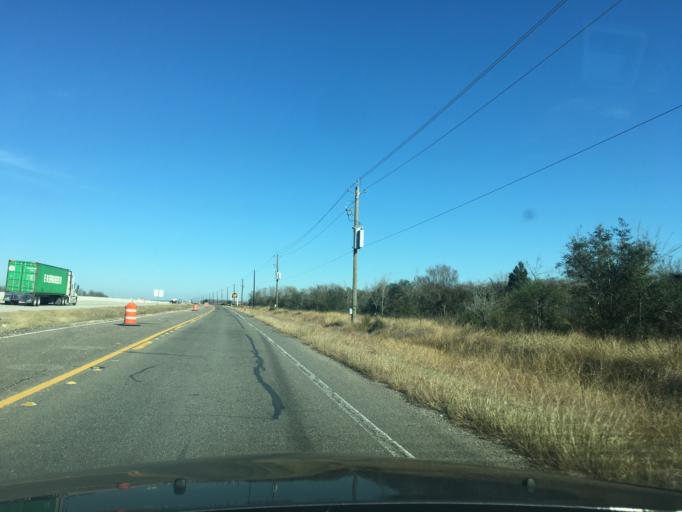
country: US
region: Texas
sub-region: Wharton County
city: East Bernard
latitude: 29.4510
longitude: -95.9900
